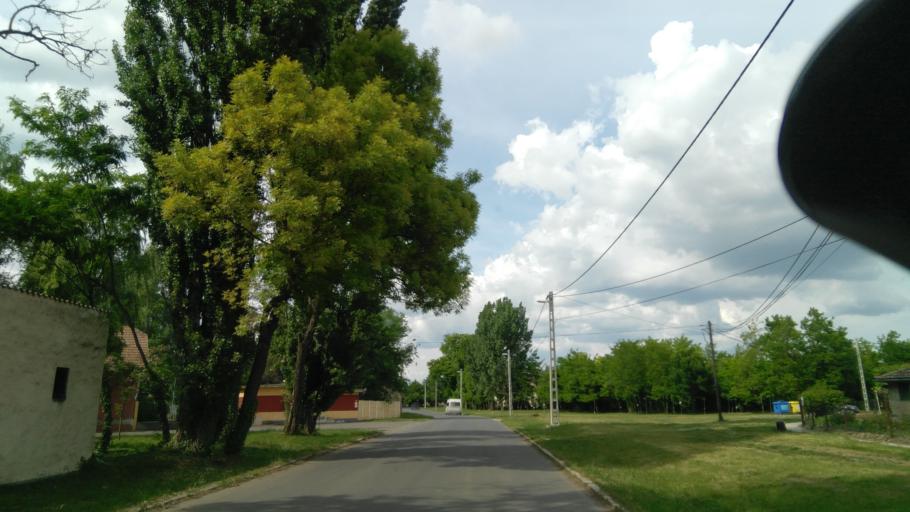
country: HU
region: Bekes
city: Mezohegyes
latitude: 46.3140
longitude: 20.8234
